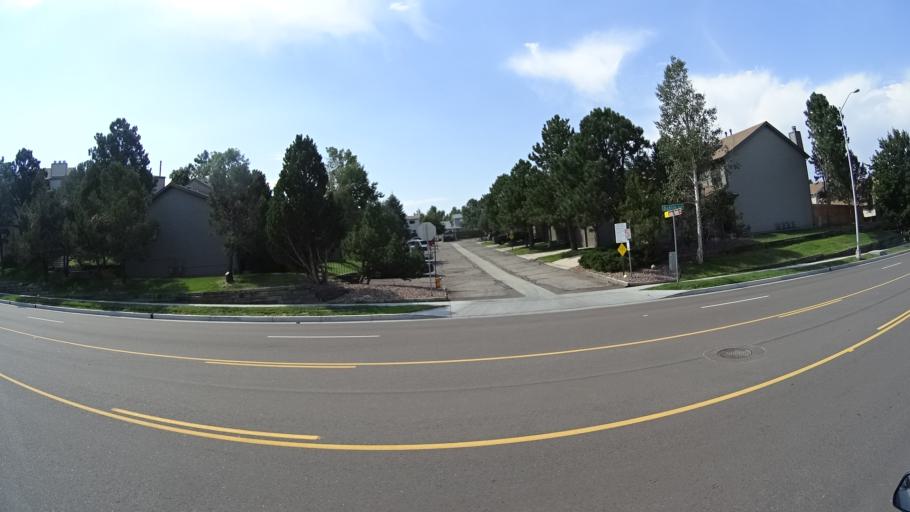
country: US
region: Colorado
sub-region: El Paso County
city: Colorado Springs
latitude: 38.9259
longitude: -104.7815
